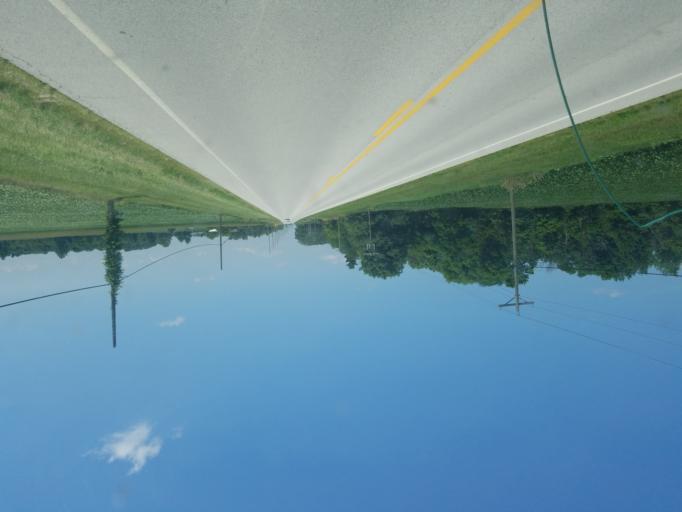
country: US
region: Ohio
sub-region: Auglaize County
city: Saint Marys
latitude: 40.5496
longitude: -84.3436
